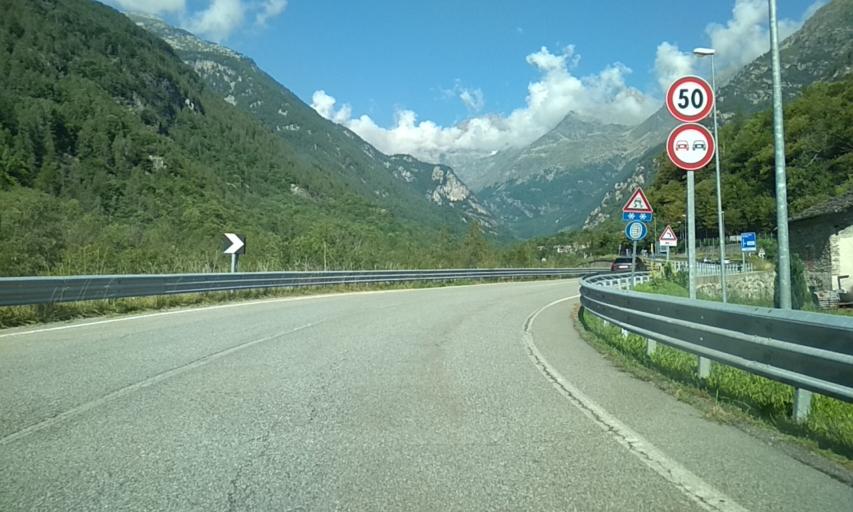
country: IT
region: Piedmont
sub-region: Provincia di Torino
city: Noasca
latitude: 45.4333
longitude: 7.3604
